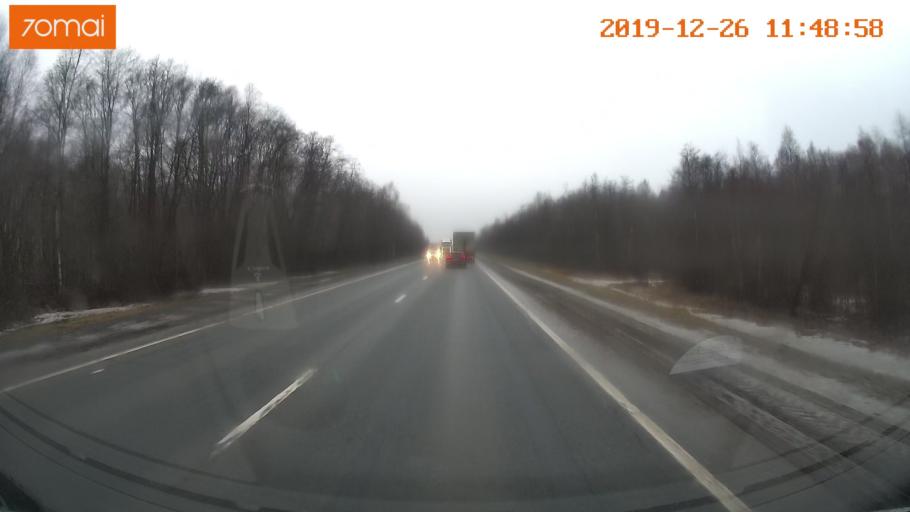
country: RU
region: Vologda
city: Sheksna
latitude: 59.2451
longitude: 38.4277
